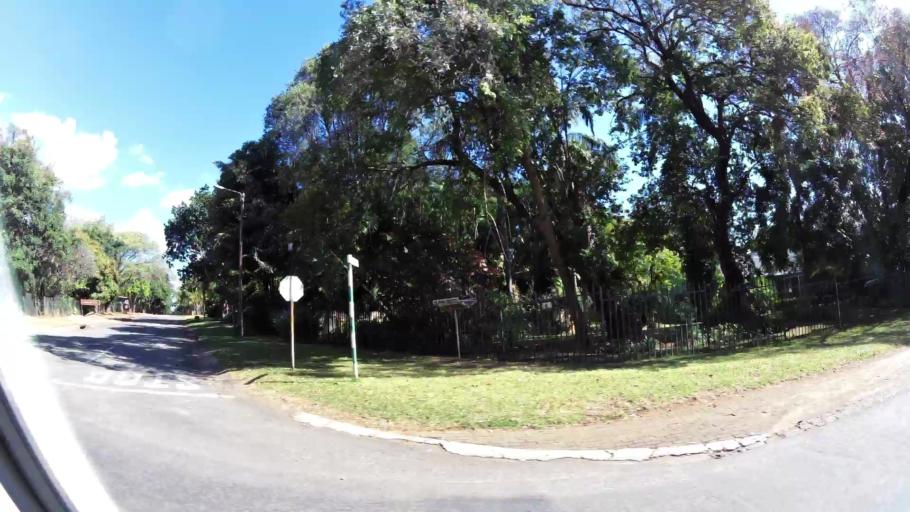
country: ZA
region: Limpopo
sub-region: Mopani District Municipality
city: Tzaneen
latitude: -23.8339
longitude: 30.1526
